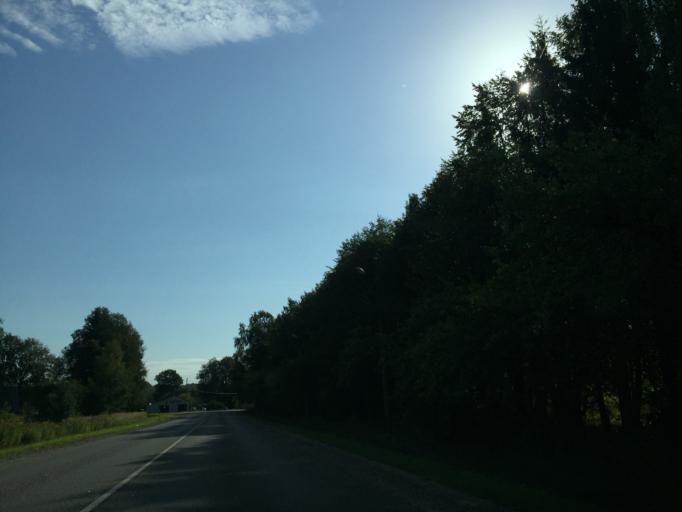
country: LV
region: Limbazu Rajons
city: Limbazi
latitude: 57.5130
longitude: 24.6879
